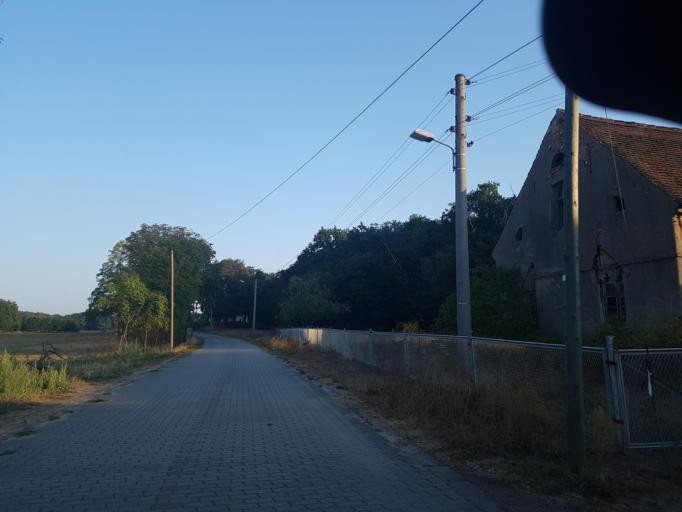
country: DE
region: Brandenburg
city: Falkenberg
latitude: 51.6438
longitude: 13.2935
